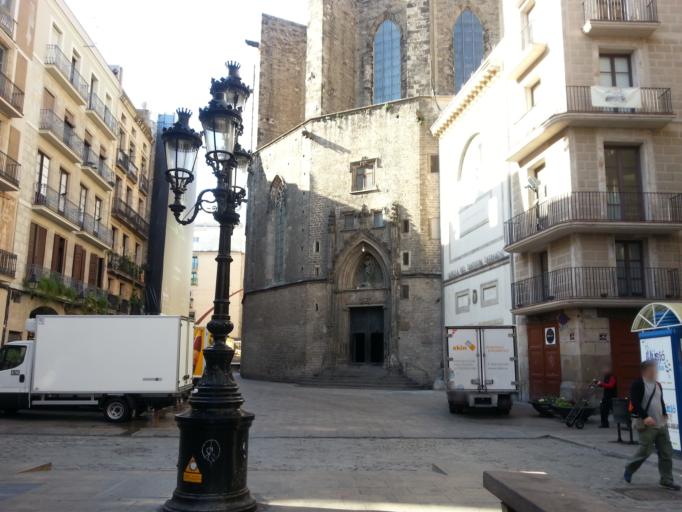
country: ES
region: Catalonia
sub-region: Provincia de Barcelona
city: Ciutat Vella
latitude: 41.3845
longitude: 2.1825
